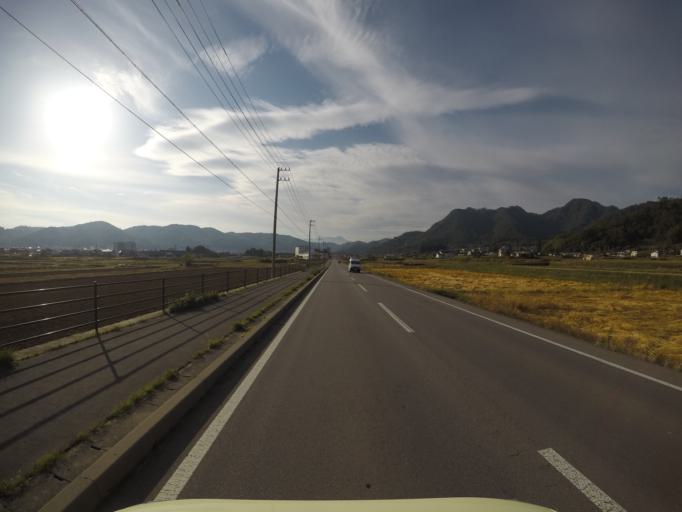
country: JP
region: Nagano
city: Kamimaruko
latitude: 36.3433
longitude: 138.2641
